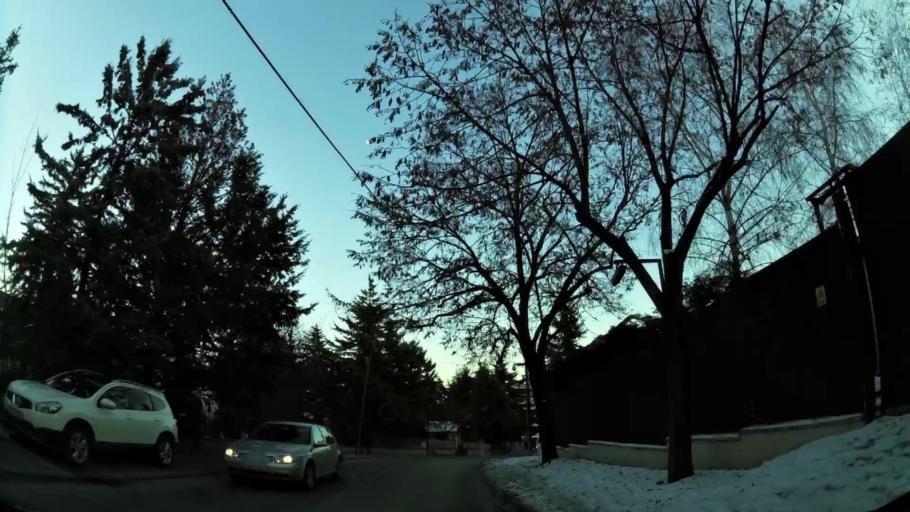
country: MK
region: Karpos
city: Skopje
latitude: 41.9883
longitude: 21.4146
